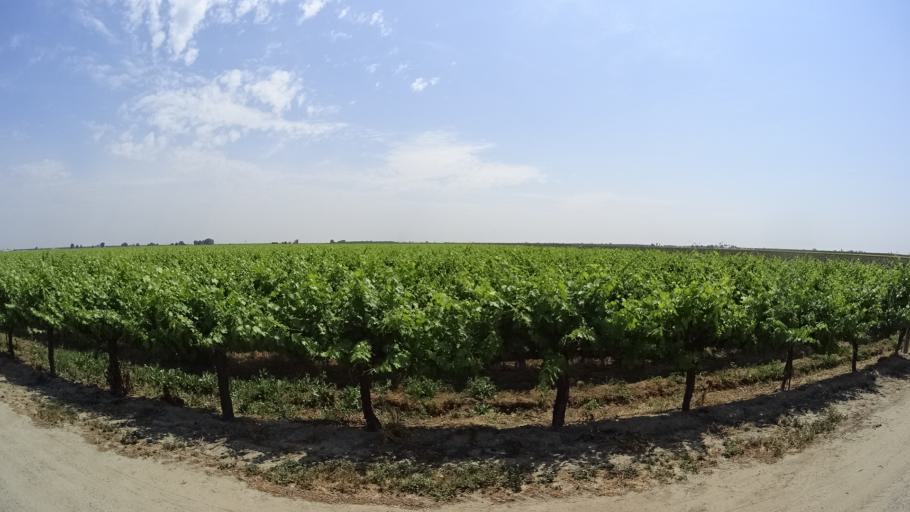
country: US
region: California
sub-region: Kings County
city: Lemoore
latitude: 36.3531
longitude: -119.7628
